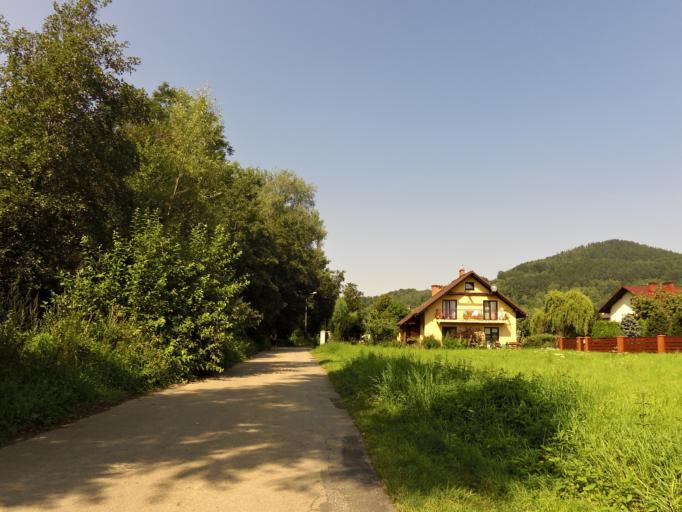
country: PL
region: Silesian Voivodeship
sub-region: Powiat zywiecki
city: Wieprz
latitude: 49.6504
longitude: 19.1792
